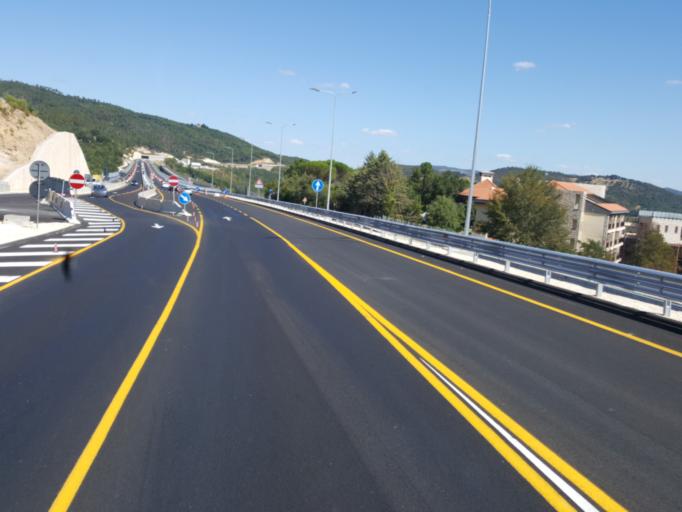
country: IT
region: Tuscany
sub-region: Provincia di Grosseto
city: Civitella Marittima
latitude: 43.0732
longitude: 11.2973
